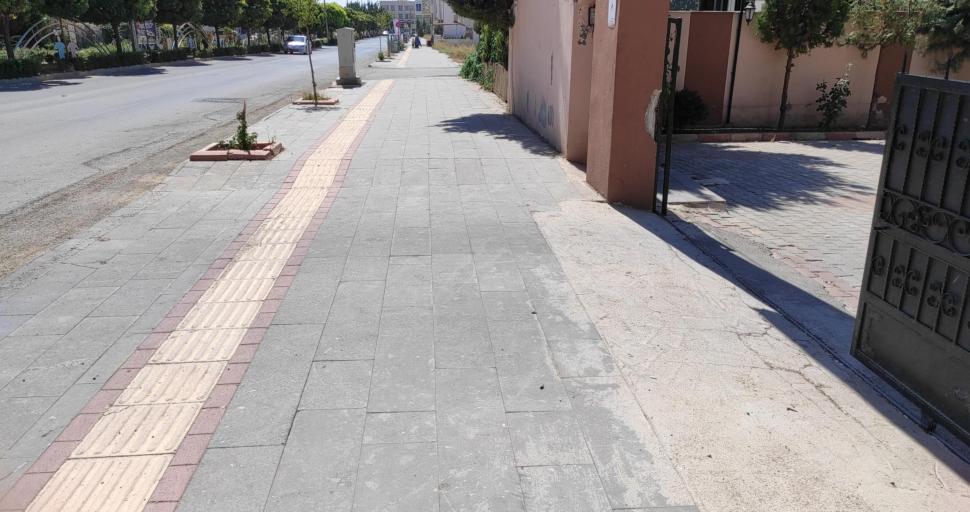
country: TR
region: Kilis
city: Kilis
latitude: 36.7254
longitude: 37.1014
